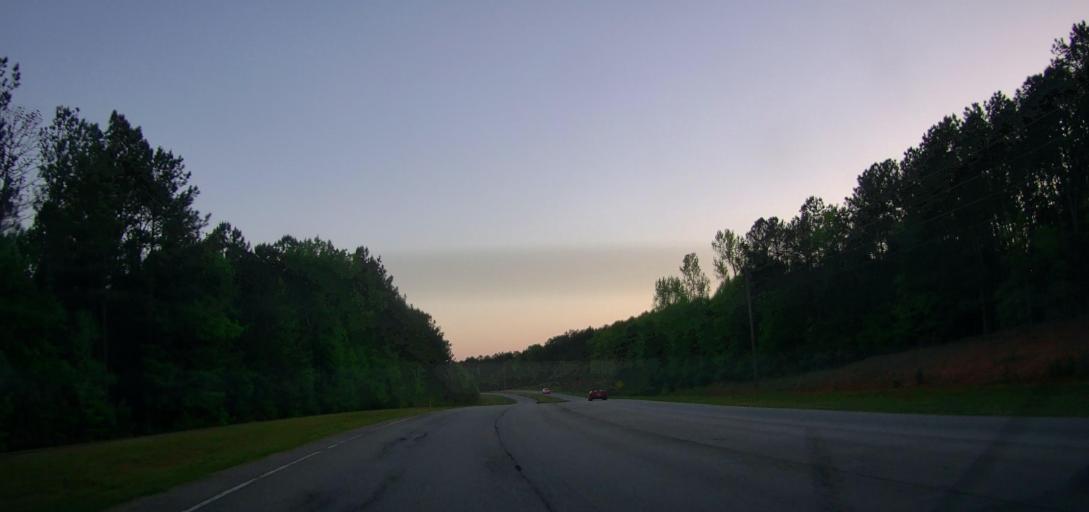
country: US
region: Georgia
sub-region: Henry County
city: McDonough
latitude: 33.4572
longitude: -84.1929
